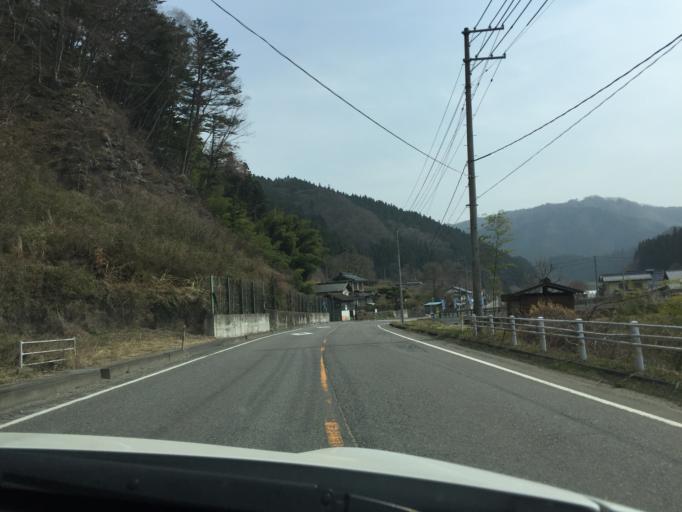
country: JP
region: Fukushima
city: Ishikawa
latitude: 37.0675
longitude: 140.5829
